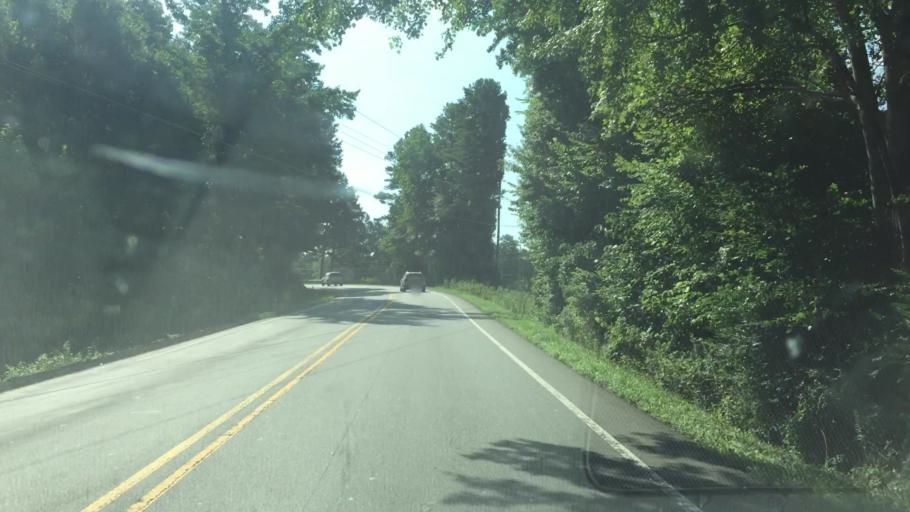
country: US
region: North Carolina
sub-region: Union County
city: Fairview
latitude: 35.1633
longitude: -80.5858
